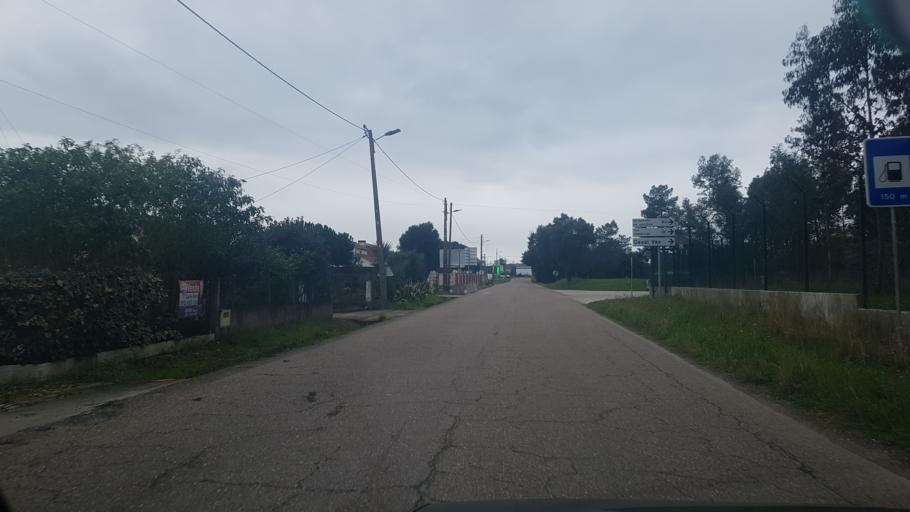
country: PT
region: Santarem
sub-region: Entroncamento
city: Entroncamento
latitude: 39.4617
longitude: -8.4909
